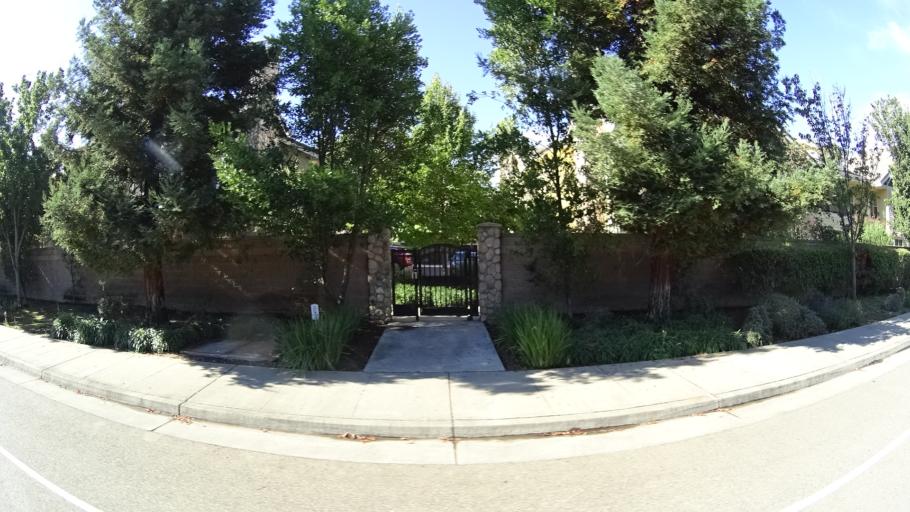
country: US
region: California
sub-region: Sacramento County
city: Laguna
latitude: 38.4104
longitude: -121.4752
